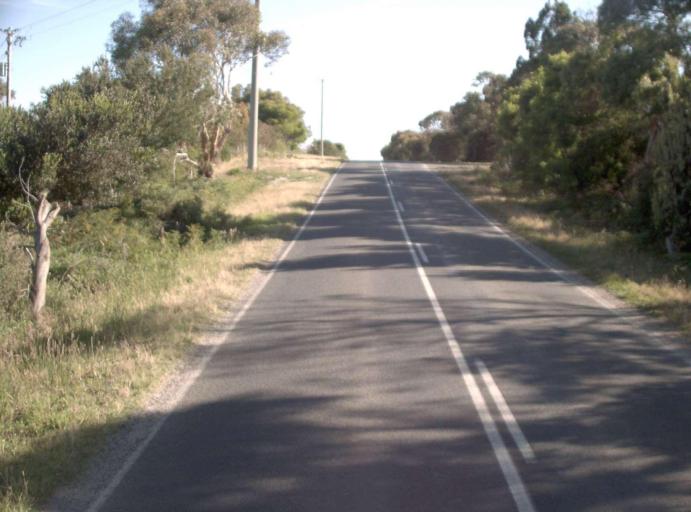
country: AU
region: Victoria
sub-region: Latrobe
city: Morwell
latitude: -38.7070
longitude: 146.3974
